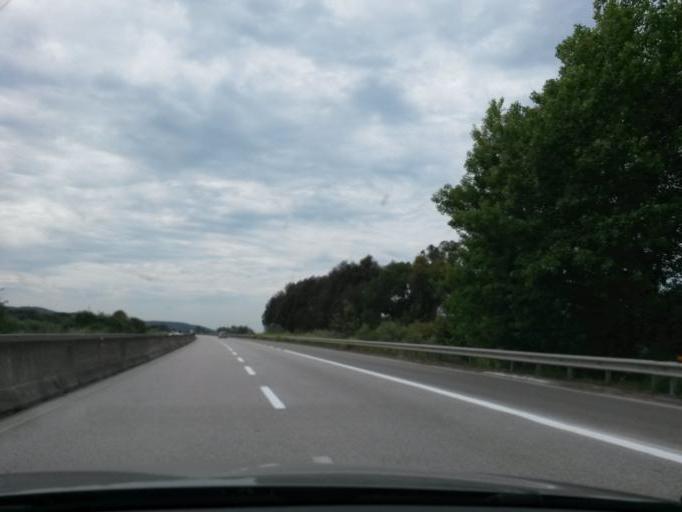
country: IT
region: Tuscany
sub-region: Provincia di Livorno
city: Donoratico
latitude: 43.1754
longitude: 10.5637
